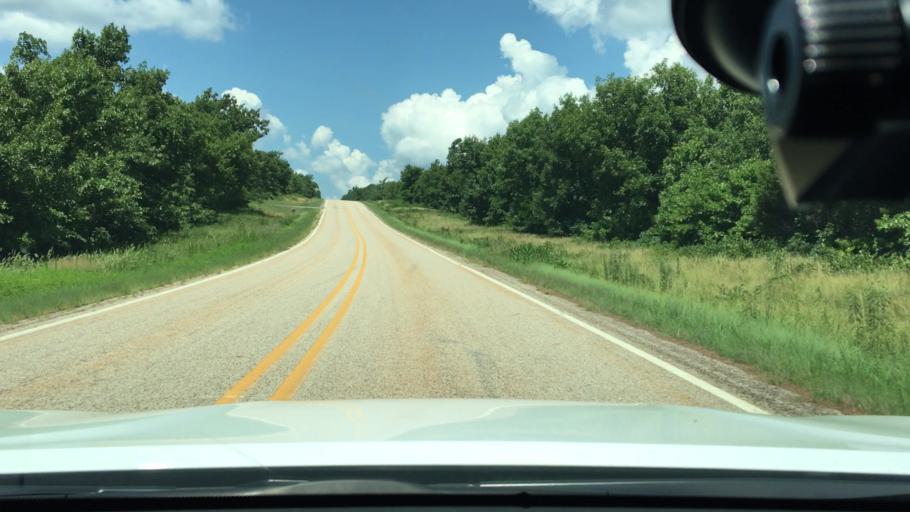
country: US
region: Arkansas
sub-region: Logan County
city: Paris
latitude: 35.1772
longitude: -93.6037
